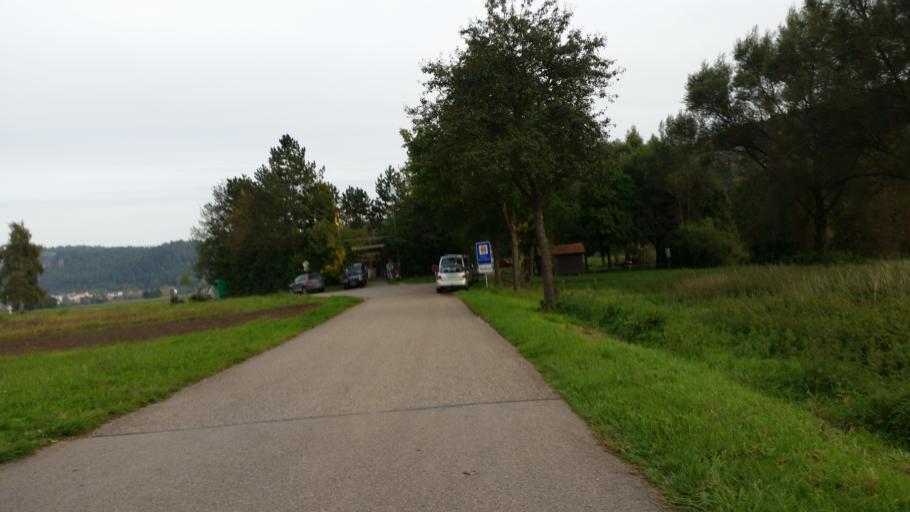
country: DE
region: Bavaria
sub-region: Upper Bavaria
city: Bohmfeld
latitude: 48.9218
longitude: 11.3583
